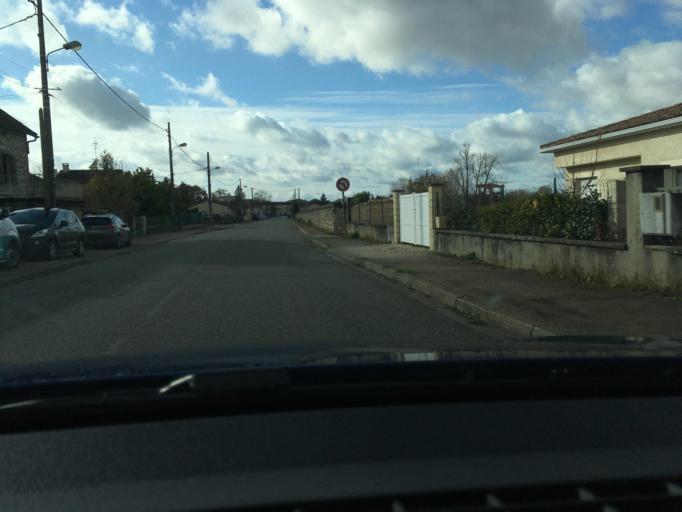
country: FR
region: Midi-Pyrenees
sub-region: Departement du Tarn-et-Garonne
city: Caussade
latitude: 44.1640
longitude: 1.5443
